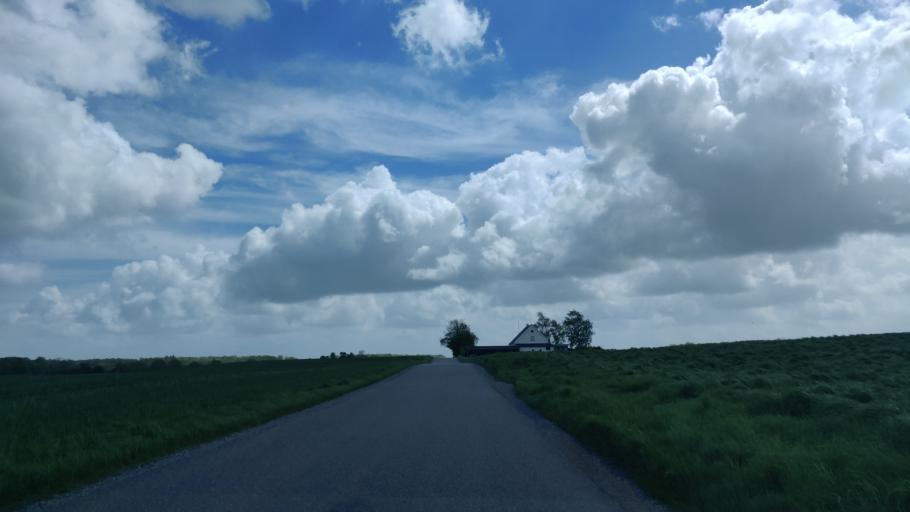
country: DK
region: South Denmark
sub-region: Vejle Kommune
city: Vejle
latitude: 55.6565
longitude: 9.5233
